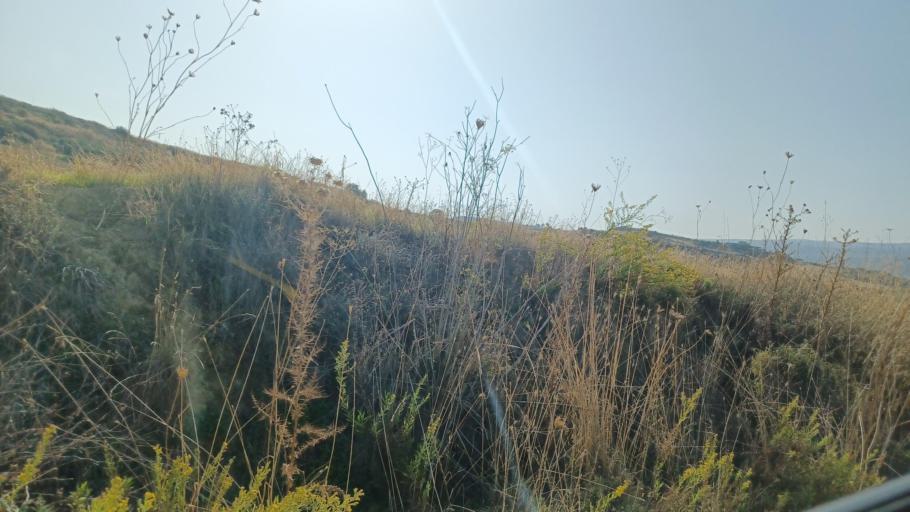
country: CY
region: Pafos
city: Polis
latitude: 35.0158
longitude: 32.4460
